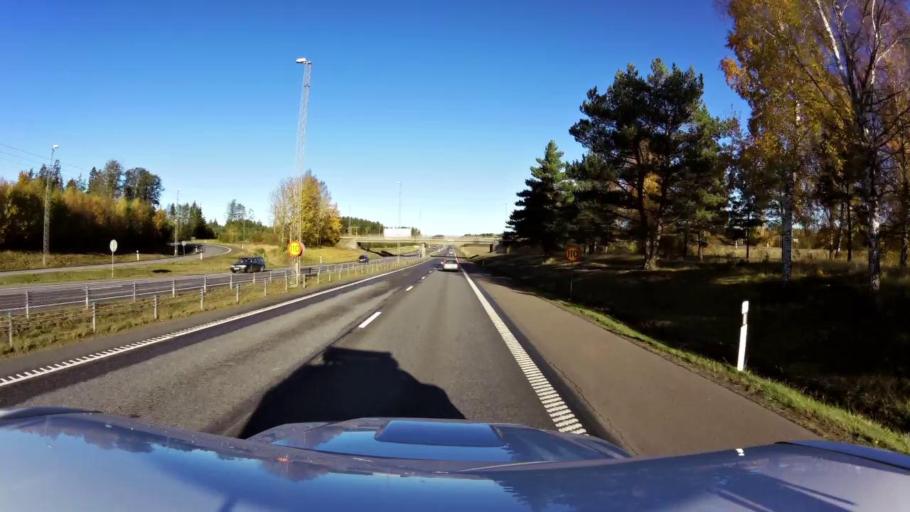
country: SE
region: OEstergoetland
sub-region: Linkopings Kommun
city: Malmslatt
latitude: 58.4107
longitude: 15.5488
